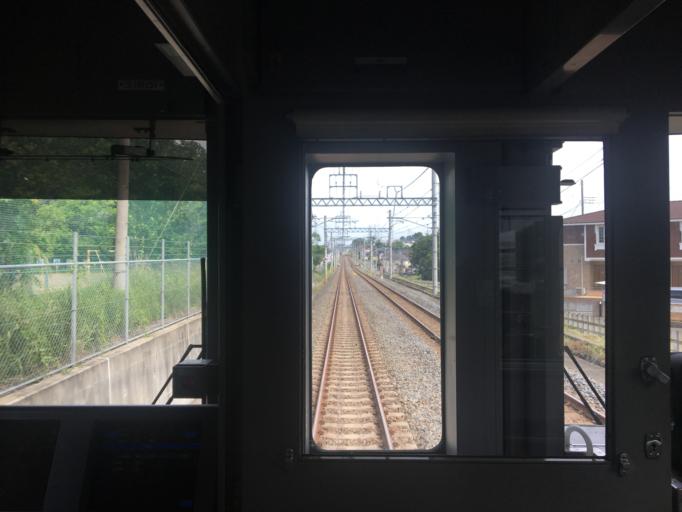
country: JP
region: Saitama
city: Ogawa
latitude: 36.0483
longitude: 139.3195
